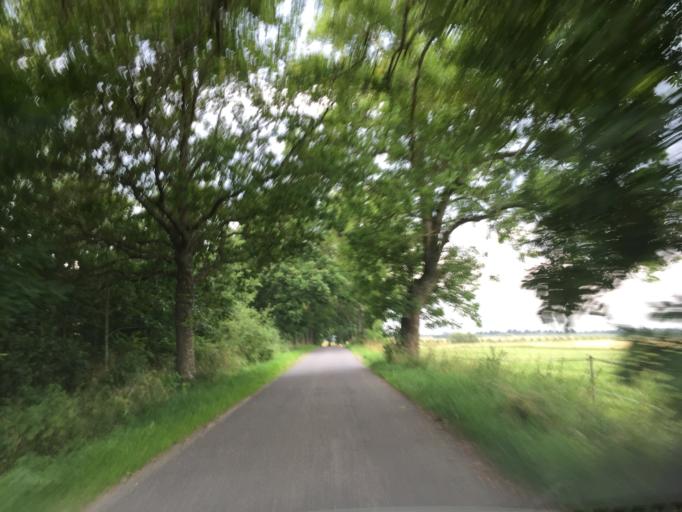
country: DK
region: Central Jutland
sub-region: Viborg Kommune
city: Bjerringbro
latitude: 56.3261
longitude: 9.6606
